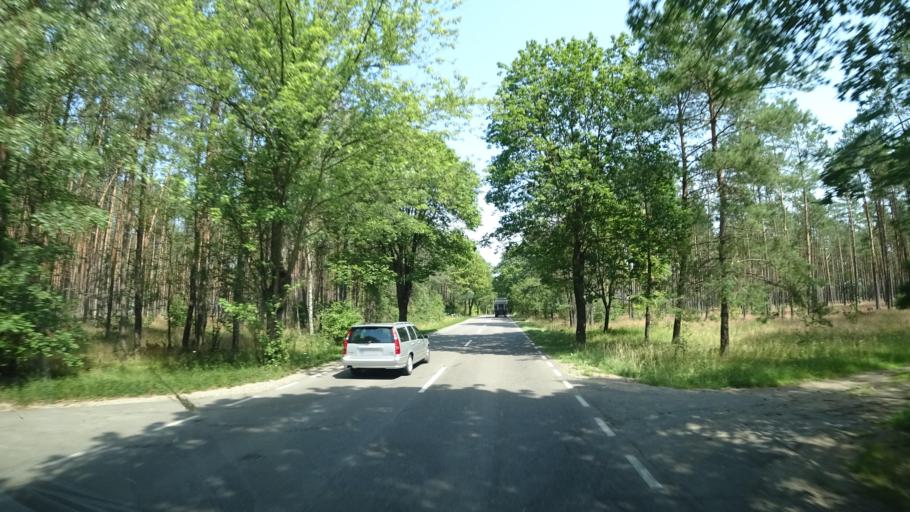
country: PL
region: Pomeranian Voivodeship
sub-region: Powiat koscierski
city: Lipusz
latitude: 54.1222
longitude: 17.8486
